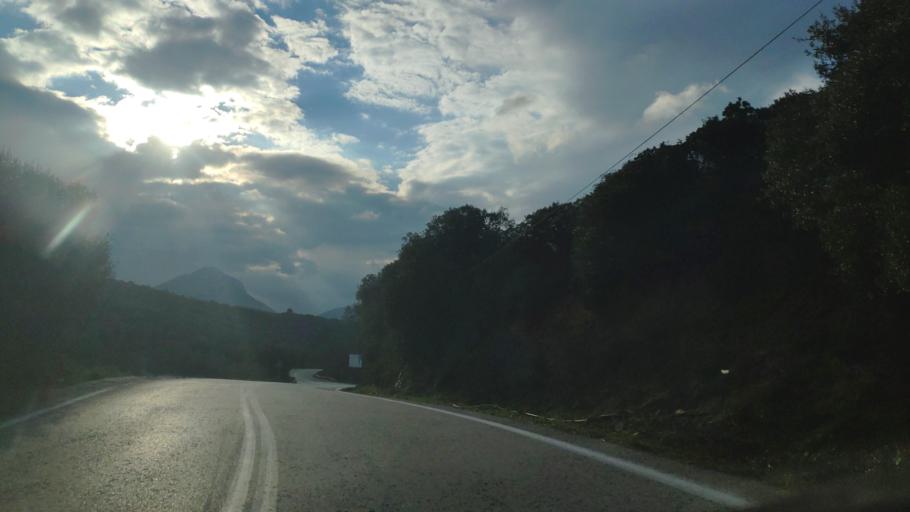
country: GR
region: Peloponnese
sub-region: Nomos Korinthias
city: Nemea
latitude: 37.7793
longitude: 22.7230
